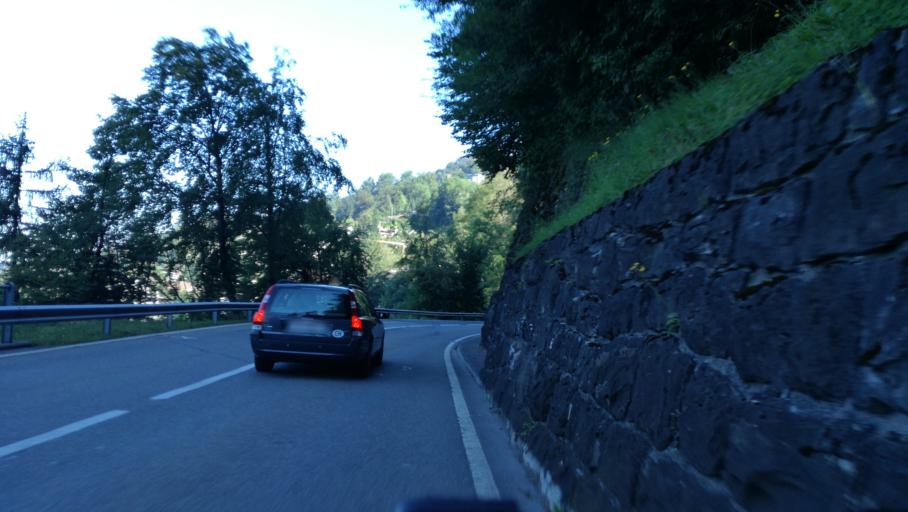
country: CH
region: Zug
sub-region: Zug
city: Walchwil
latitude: 47.0872
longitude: 8.5238
